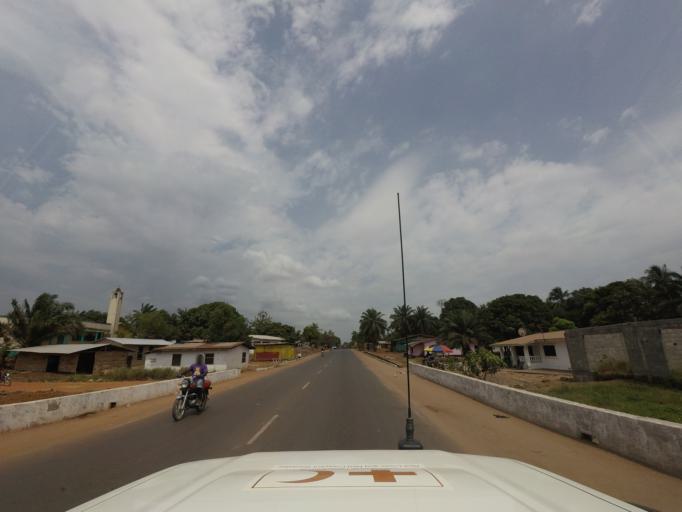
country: LR
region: Montserrado
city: Monrovia
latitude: 6.2840
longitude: -10.6837
